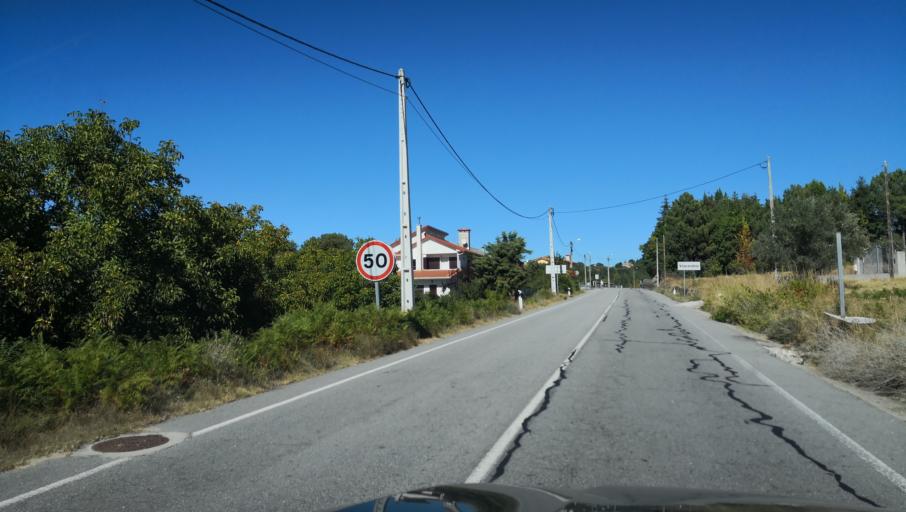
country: PT
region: Vila Real
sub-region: Valpacos
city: Valpacos
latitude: 41.6495
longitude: -7.3207
